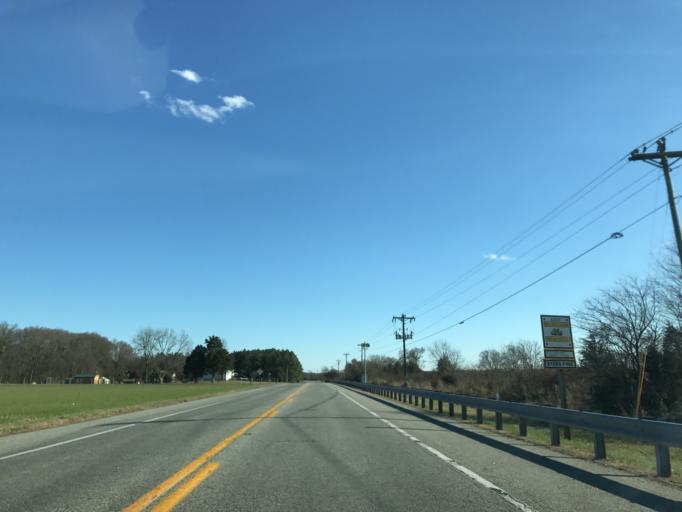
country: US
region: Maryland
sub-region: Caroline County
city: Greensboro
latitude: 39.0660
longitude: -75.8511
